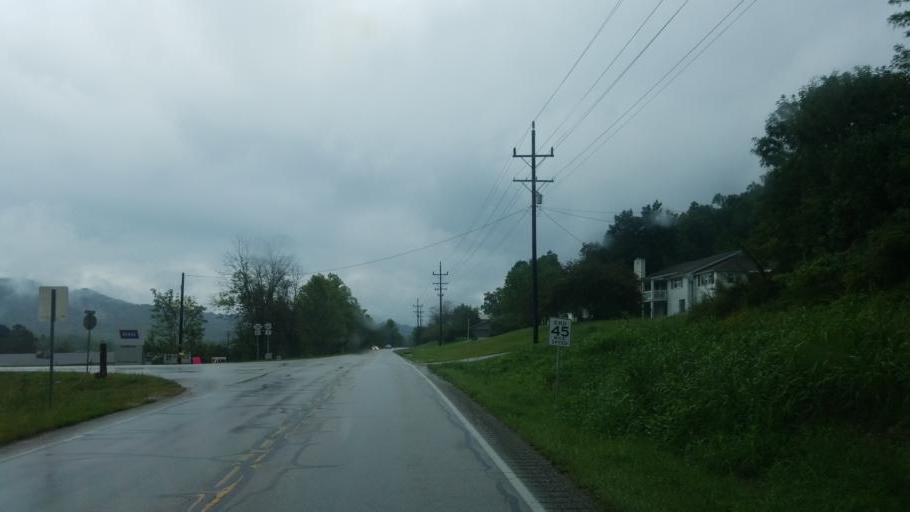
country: US
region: Kentucky
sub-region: Rowan County
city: Morehead
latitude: 38.1586
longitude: -83.4562
